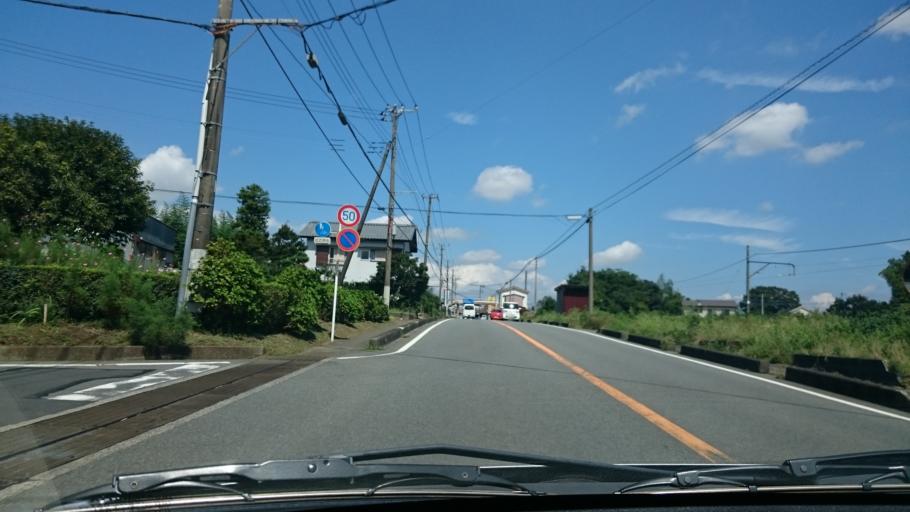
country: JP
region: Shizuoka
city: Gotemba
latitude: 35.2739
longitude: 138.9240
